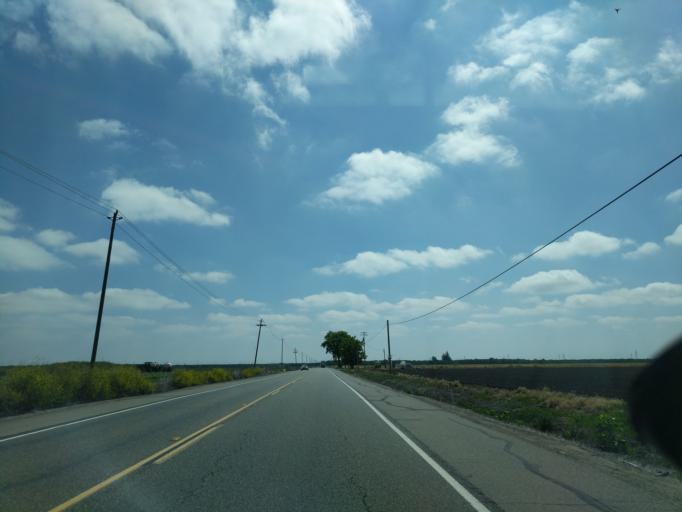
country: US
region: California
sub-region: San Joaquin County
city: Garden Acres
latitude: 37.9490
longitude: -121.1778
